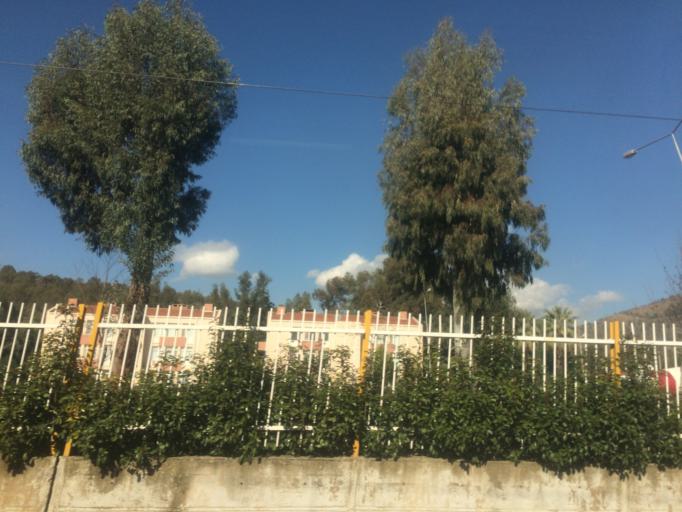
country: TR
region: Izmir
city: Karsiyaka
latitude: 38.4662
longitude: 27.1464
